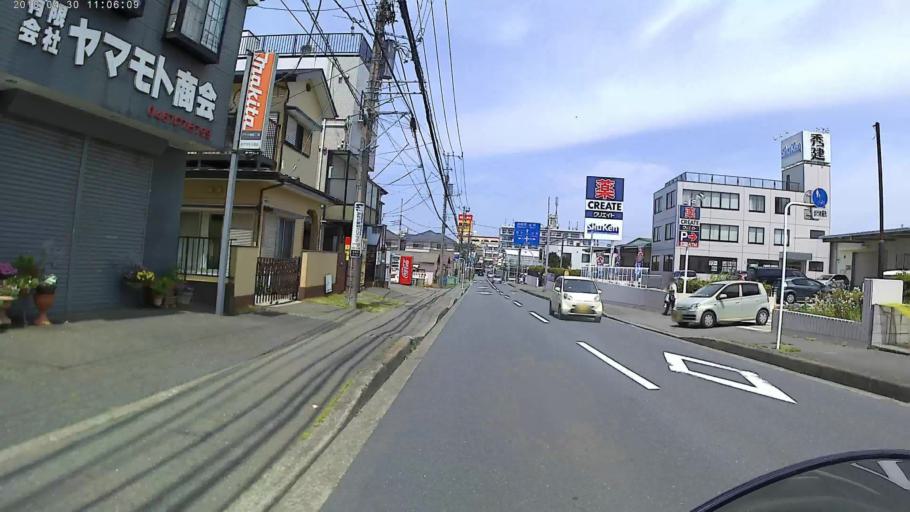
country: JP
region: Kanagawa
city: Minami-rinkan
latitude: 35.4540
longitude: 139.4288
